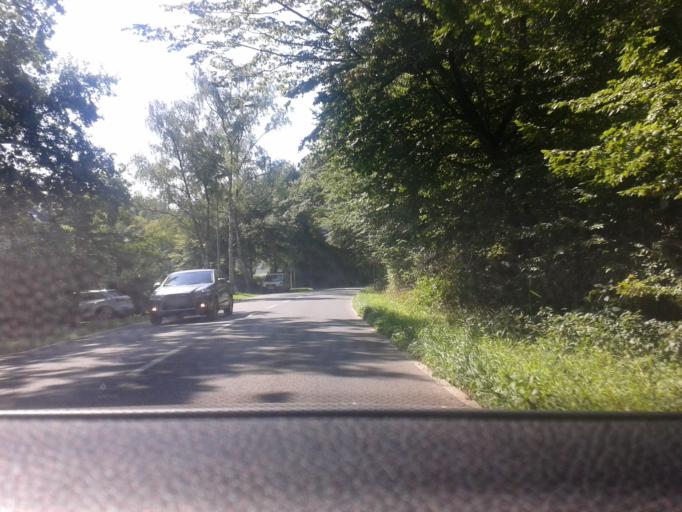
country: DE
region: North Rhine-Westphalia
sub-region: Regierungsbezirk Dusseldorf
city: Muelheim (Ruhr)
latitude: 51.4051
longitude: 6.8494
